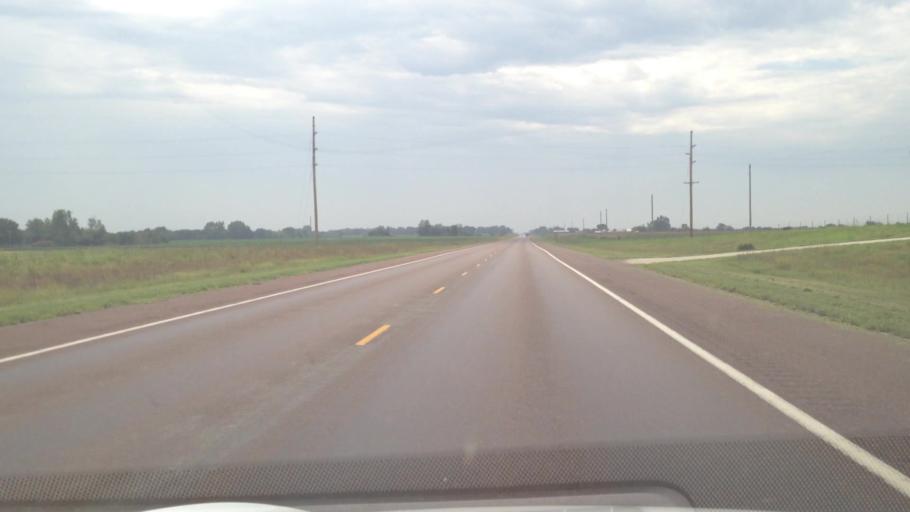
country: US
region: Kansas
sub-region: Crawford County
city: Girard
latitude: 37.4581
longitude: -94.8330
